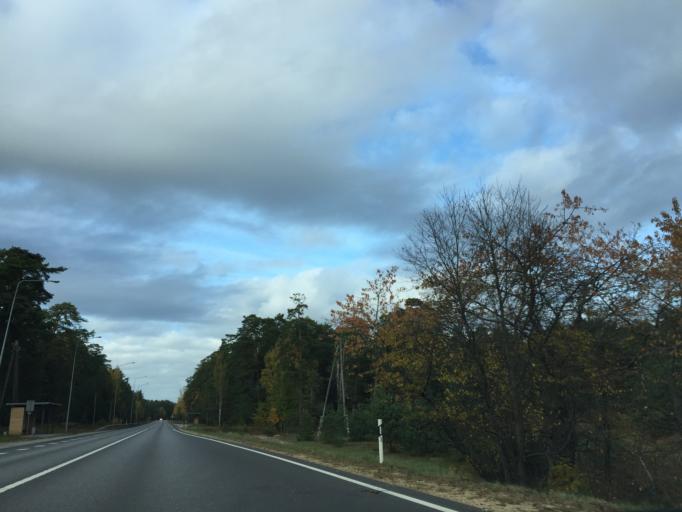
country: LV
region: Salacgrivas
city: Salacgriva
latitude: 57.6378
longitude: 24.3771
